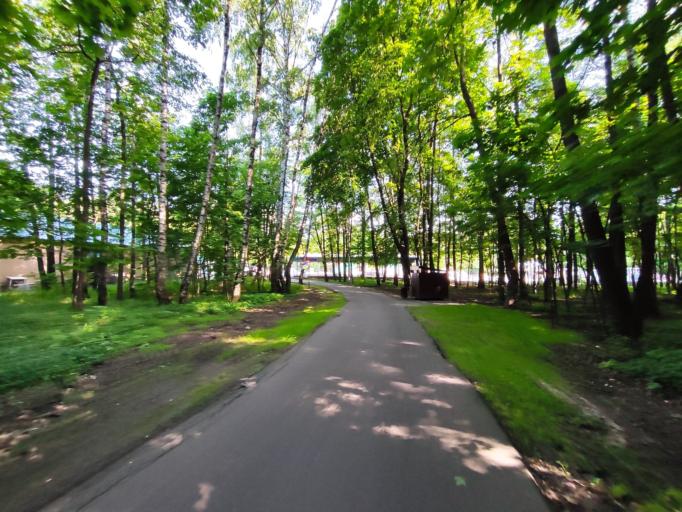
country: RU
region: Moscow
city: Metrogorodok
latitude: 55.7848
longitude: 37.7527
